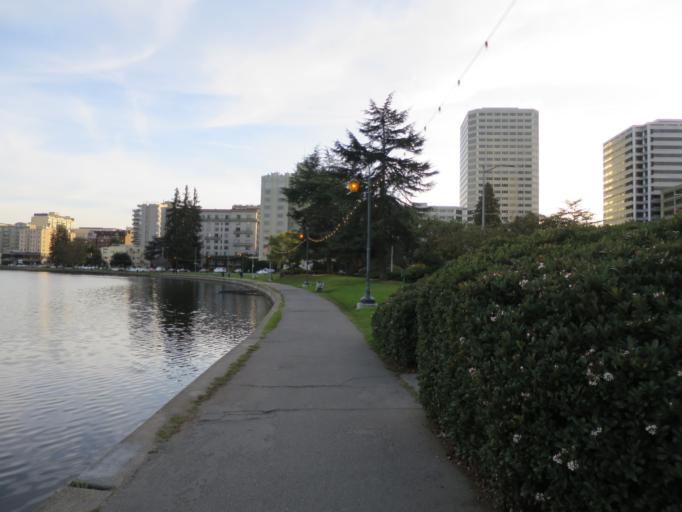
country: US
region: California
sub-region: Alameda County
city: Oakland
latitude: 37.8084
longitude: -122.2630
